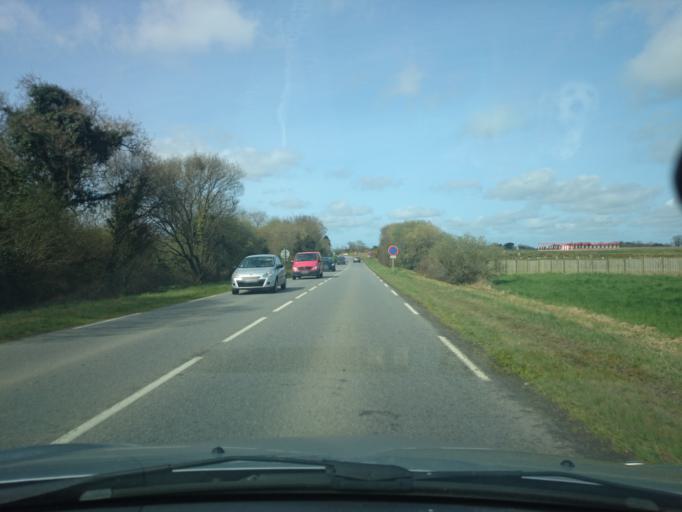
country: FR
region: Brittany
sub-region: Departement du Finistere
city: Gouesnou
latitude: 48.4412
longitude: -4.4400
